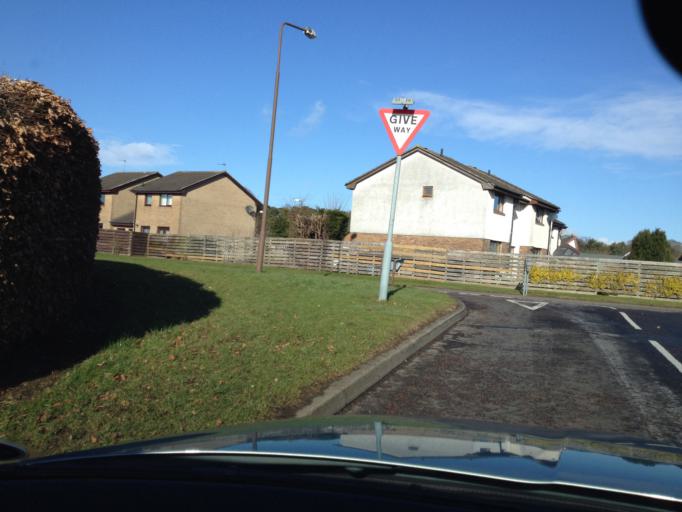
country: GB
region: Scotland
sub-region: West Lothian
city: Livingston
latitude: 55.8870
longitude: -3.5385
